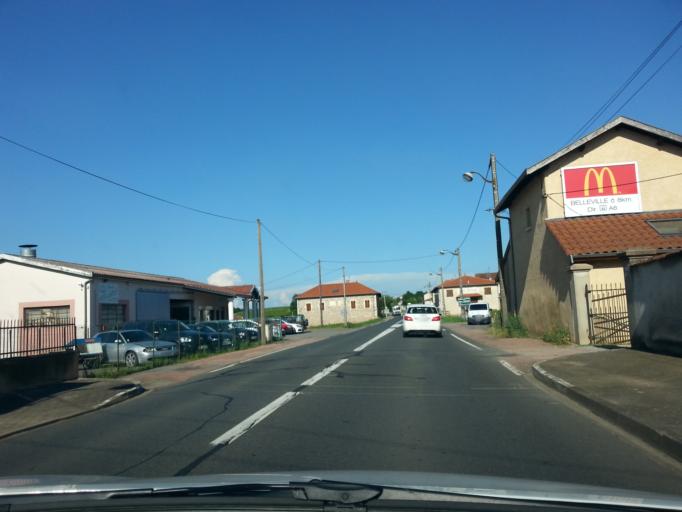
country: FR
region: Rhone-Alpes
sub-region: Departement du Rhone
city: Charentay
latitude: 46.1196
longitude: 4.6735
